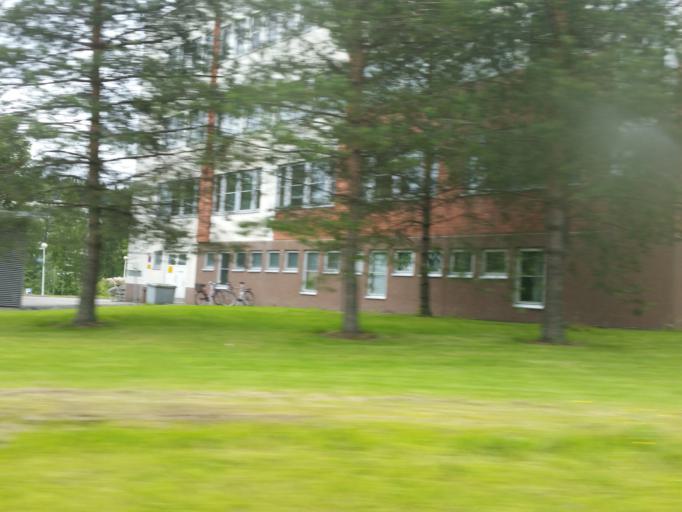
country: FI
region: Northern Savo
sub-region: Kuopio
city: Kuopio
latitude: 62.8914
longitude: 27.6368
